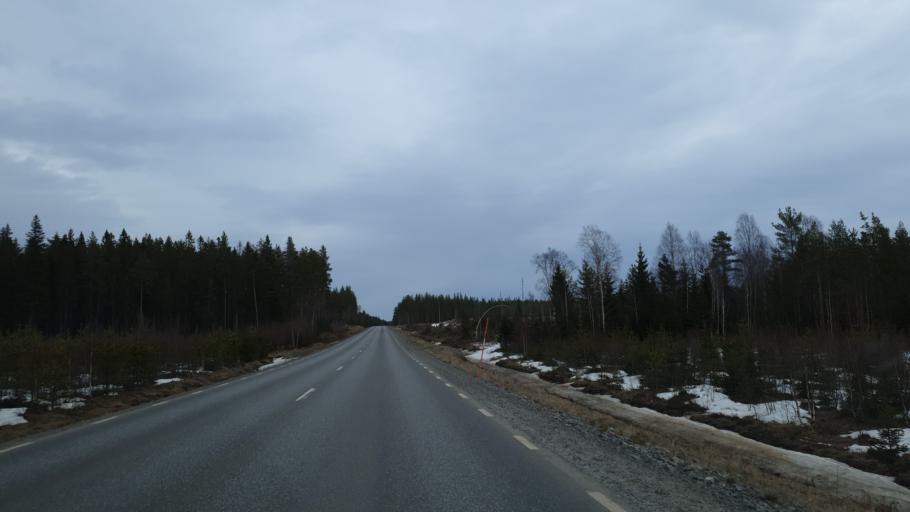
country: SE
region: Vaesterbotten
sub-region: Robertsfors Kommun
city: Robertsfors
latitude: 64.2092
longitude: 20.8771
